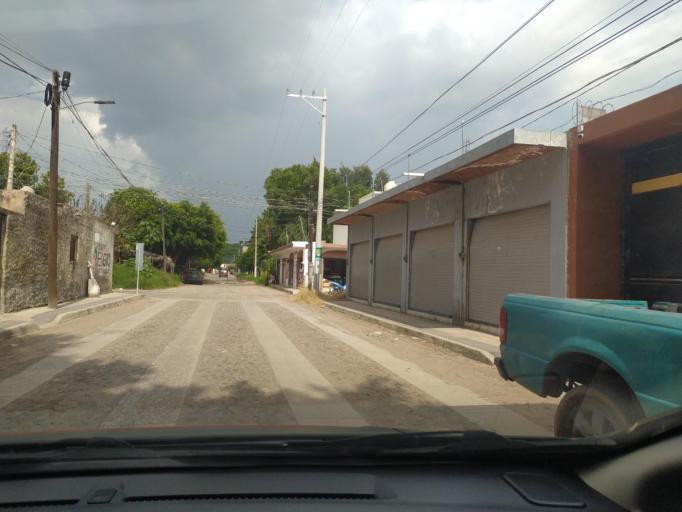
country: MX
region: Jalisco
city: Villa Corona
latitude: 20.4123
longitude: -103.6671
